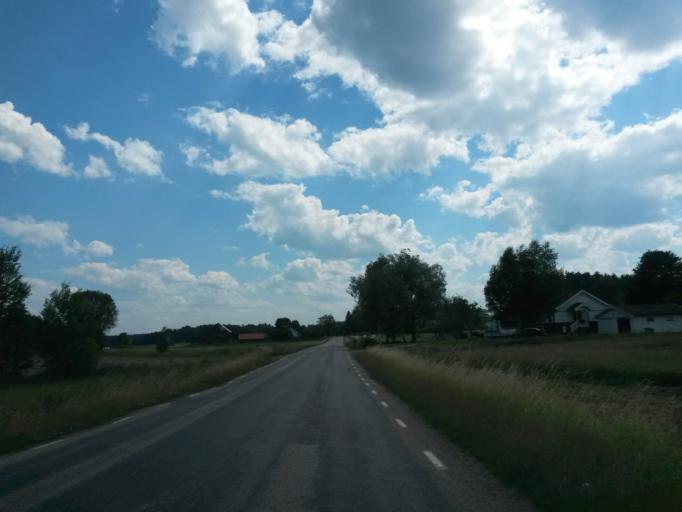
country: SE
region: Vaestra Goetaland
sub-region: Essunga Kommun
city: Nossebro
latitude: 58.1344
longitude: 12.7755
